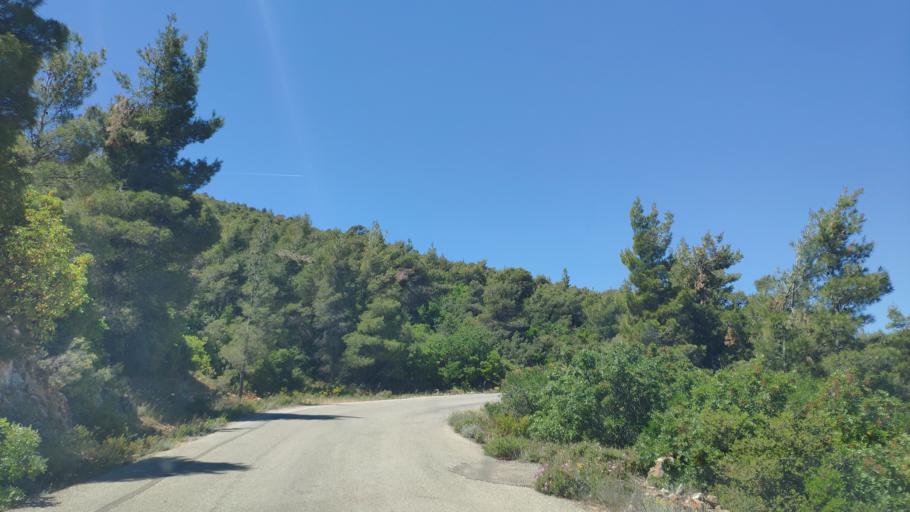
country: GR
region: Central Greece
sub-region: Nomos Voiotias
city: Kaparellion
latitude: 38.2015
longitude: 23.1585
